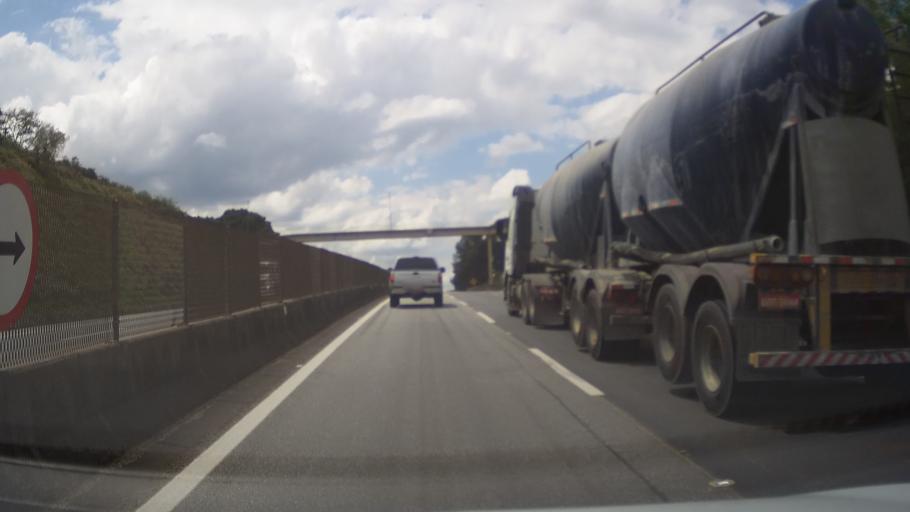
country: BR
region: Minas Gerais
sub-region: Nepomuceno
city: Nepomuceno
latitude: -21.2808
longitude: -45.1399
